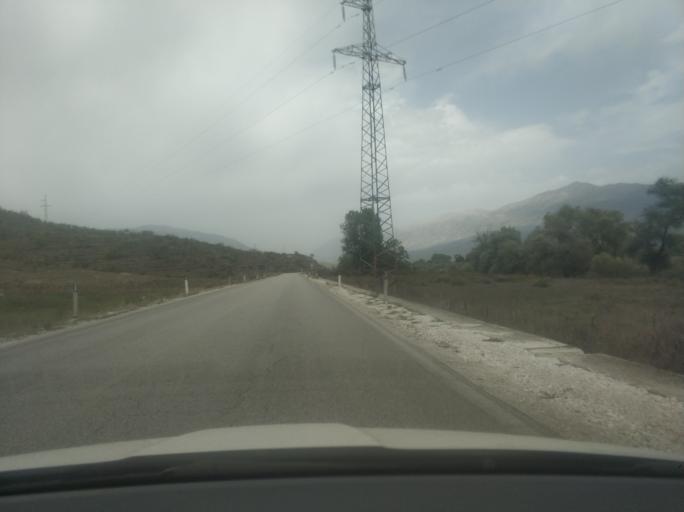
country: AL
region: Gjirokaster
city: Gjirokaster
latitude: 40.1046
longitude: 20.1235
